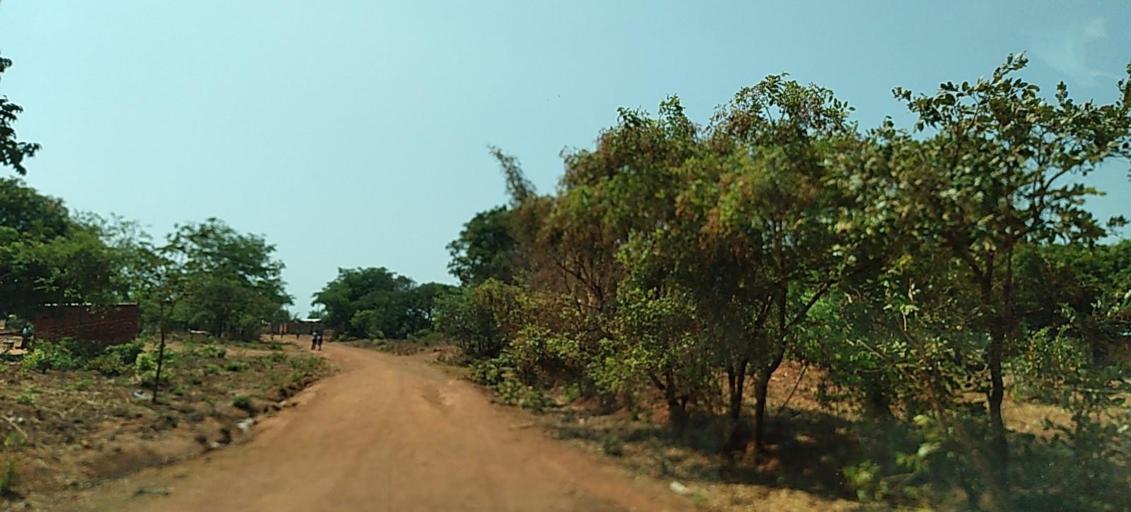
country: ZM
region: Copperbelt
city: Luanshya
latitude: -13.3512
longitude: 28.4060
